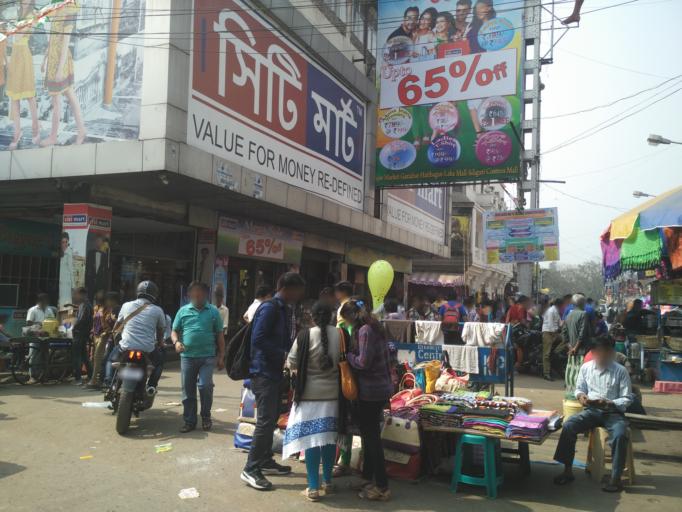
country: IN
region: West Bengal
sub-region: Kolkata
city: Bara Bazar
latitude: 22.5606
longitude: 88.3521
